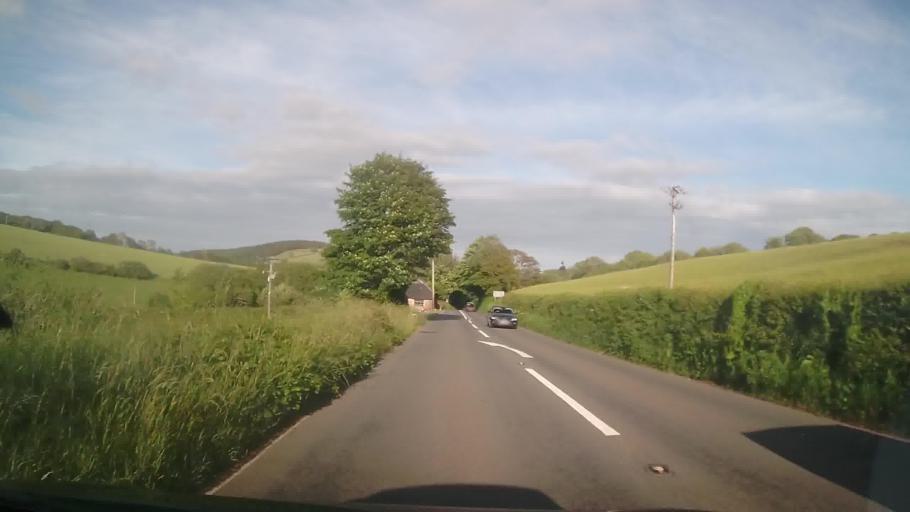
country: GB
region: England
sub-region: Devon
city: Ivybridge
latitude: 50.3525
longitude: -3.9348
